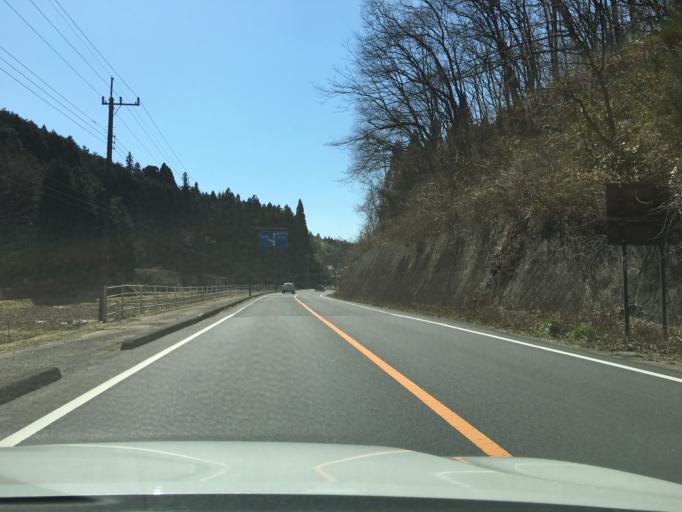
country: JP
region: Tochigi
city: Kuroiso
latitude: 37.0580
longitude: 140.1775
